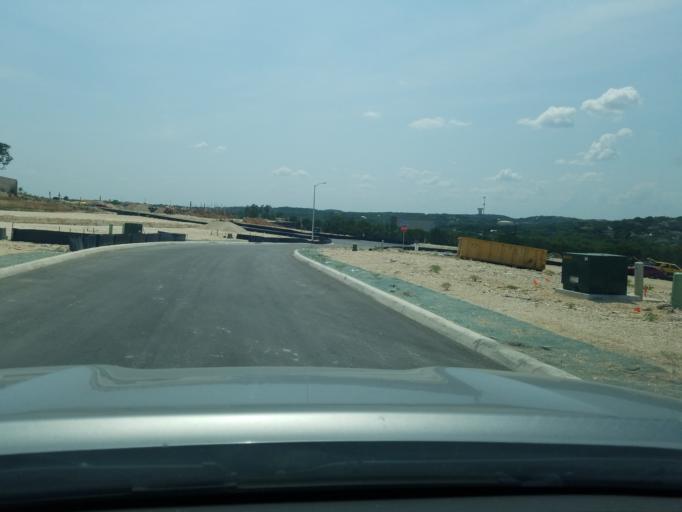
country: US
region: Texas
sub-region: Bexar County
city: Timberwood Park
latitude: 29.6830
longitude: -98.4801
